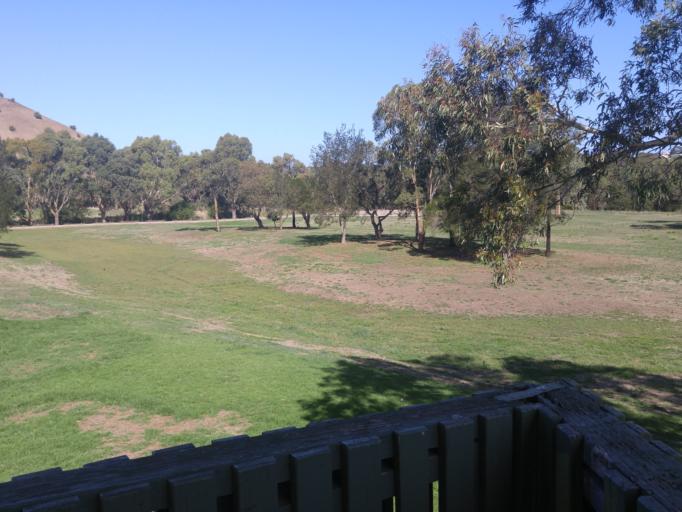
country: AU
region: Victoria
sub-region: Greater Geelong
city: Hamlyn Heights
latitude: -38.1426
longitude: 144.3109
